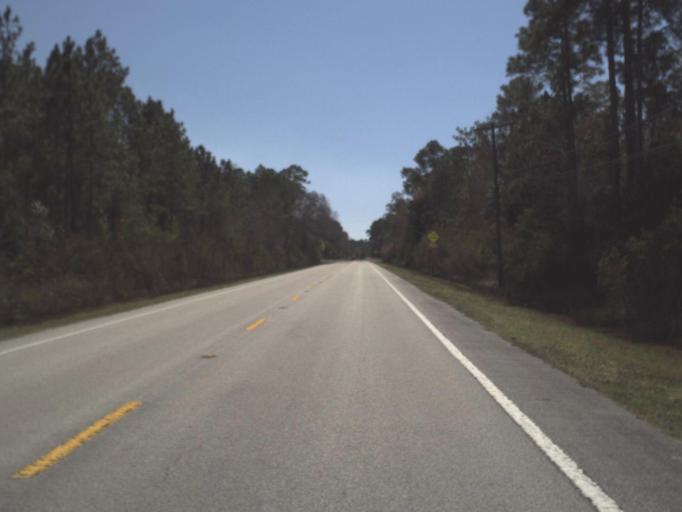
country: US
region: Florida
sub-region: Leon County
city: Woodville
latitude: 30.1791
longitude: -84.2118
